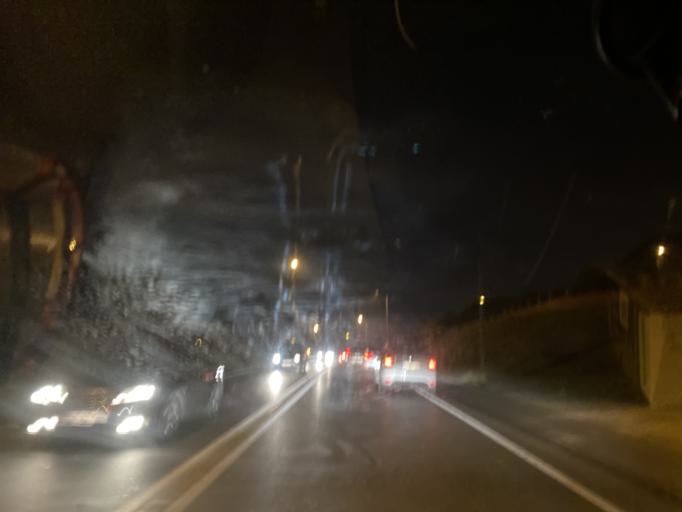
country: TR
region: Istanbul
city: Esenyurt
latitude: 41.0560
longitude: 28.7263
